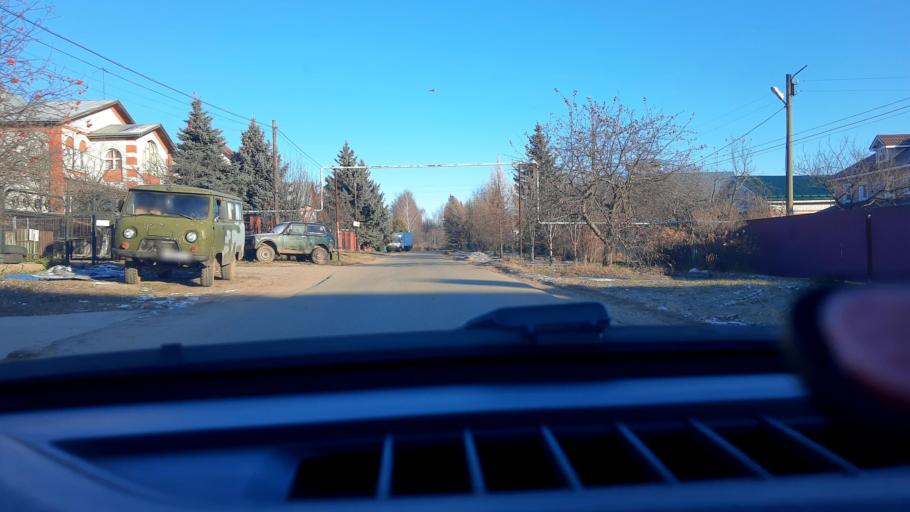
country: RU
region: Nizjnij Novgorod
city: Burevestnik
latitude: 56.2005
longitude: 43.8775
